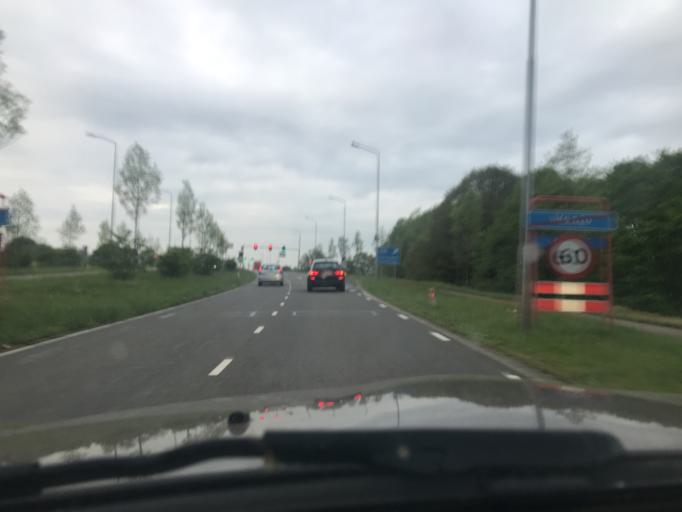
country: NL
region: Limburg
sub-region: Gemeente Venlo
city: Venlo
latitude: 51.3872
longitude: 6.1987
